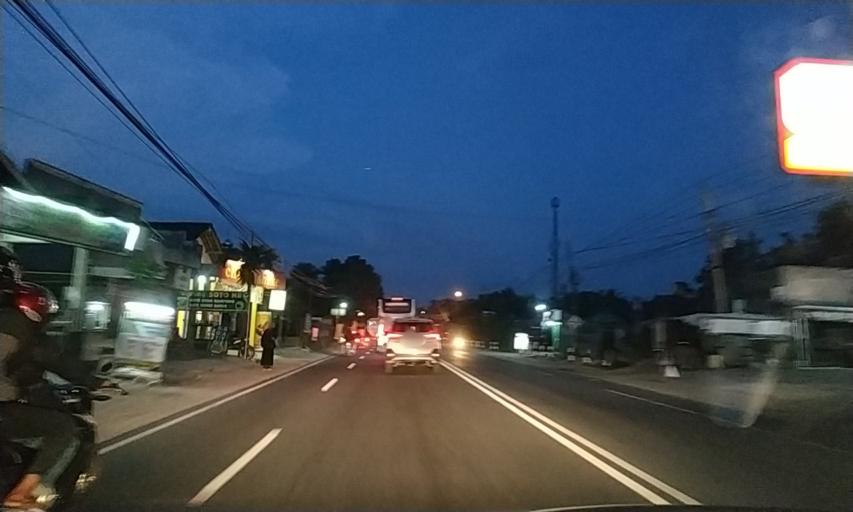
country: ID
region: Daerah Istimewa Yogyakarta
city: Godean
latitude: -7.8084
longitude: 110.2883
